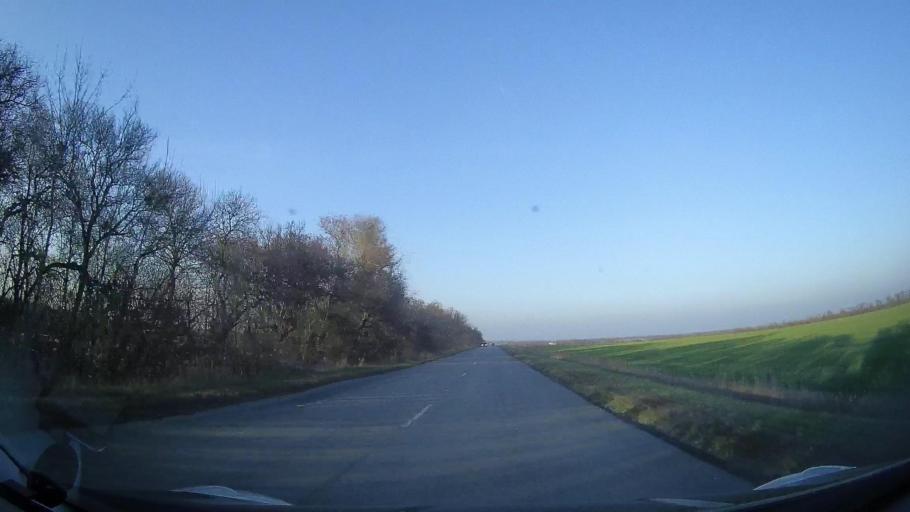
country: RU
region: Rostov
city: Kirovskaya
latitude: 47.0159
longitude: 39.9789
